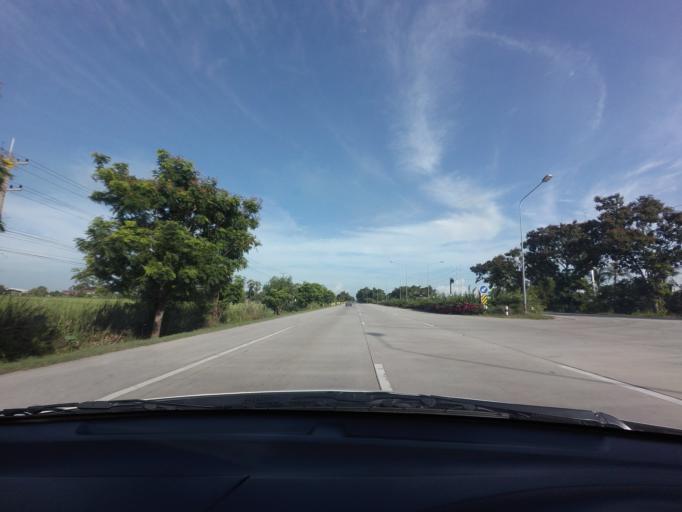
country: TH
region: Phra Nakhon Si Ayutthaya
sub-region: Amphoe Bang Sai
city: Bang Sai
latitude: 14.2786
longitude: 100.2457
